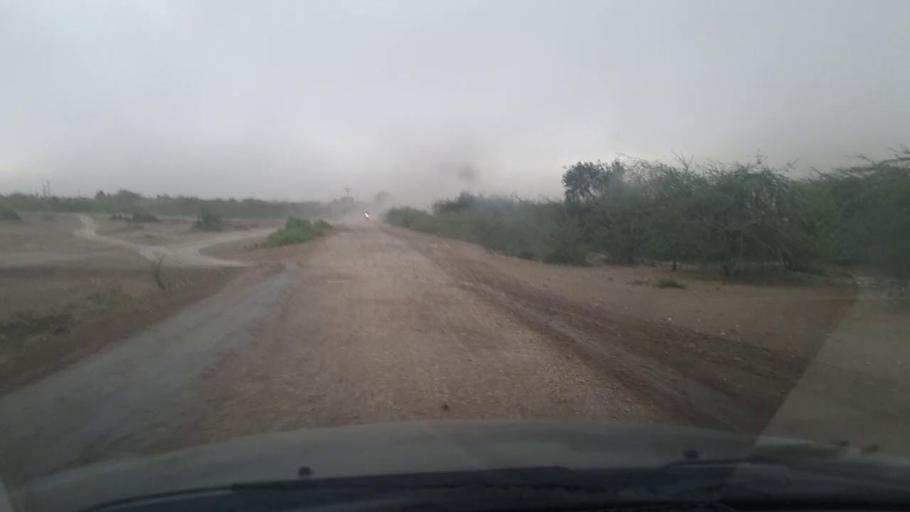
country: PK
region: Sindh
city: Digri
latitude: 25.0034
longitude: 69.0953
